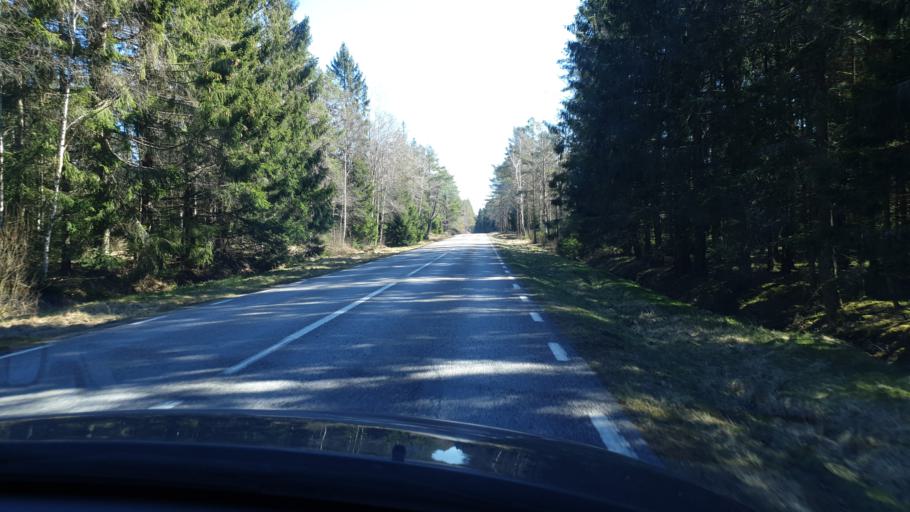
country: SE
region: Vaestra Goetaland
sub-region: Tanums Kommun
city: Tanumshede
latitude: 58.7425
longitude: 11.4617
